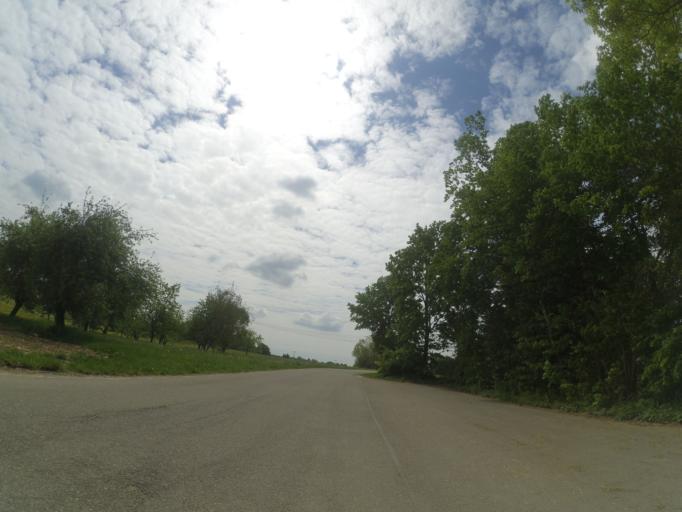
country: DE
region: Baden-Wuerttemberg
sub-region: Tuebingen Region
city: Blaubeuren
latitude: 48.4303
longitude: 9.7738
